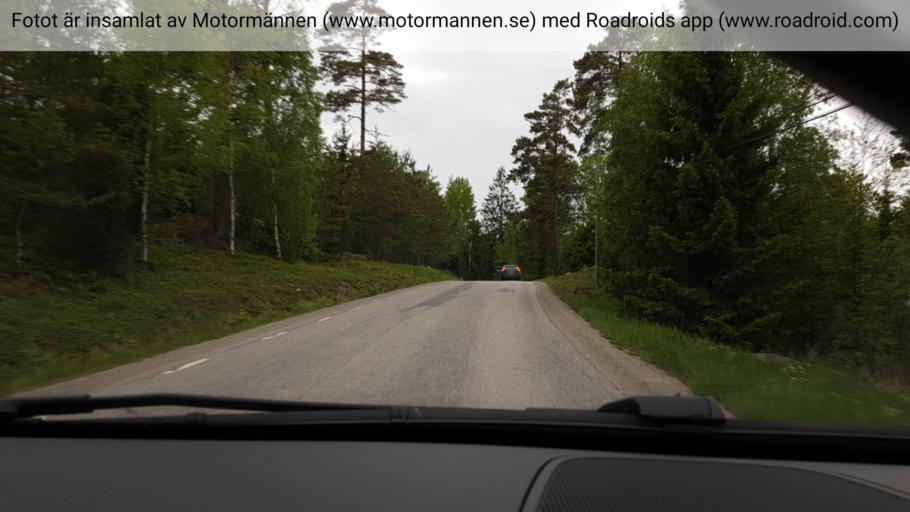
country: SE
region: Stockholm
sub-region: Nynashamns Kommun
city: Osmo
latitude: 59.0280
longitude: 17.9461
